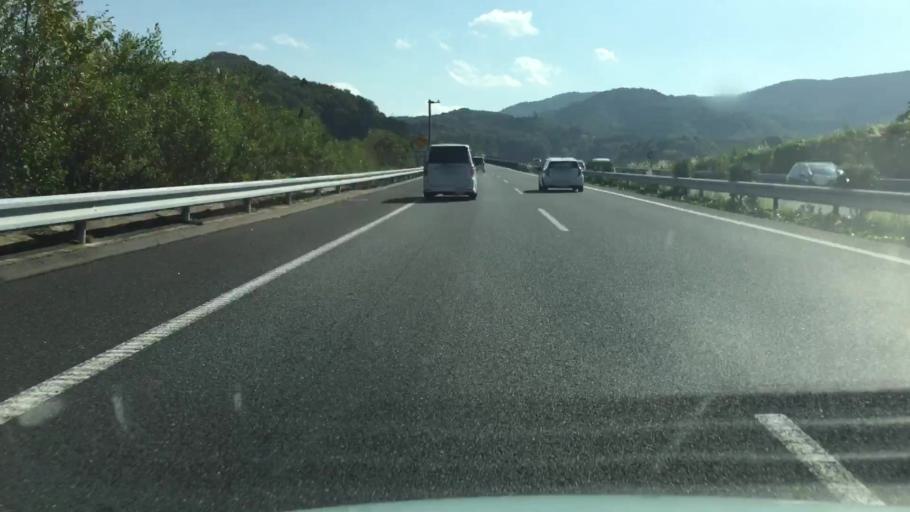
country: JP
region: Ibaraki
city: Iwase
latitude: 36.3431
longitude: 140.1847
